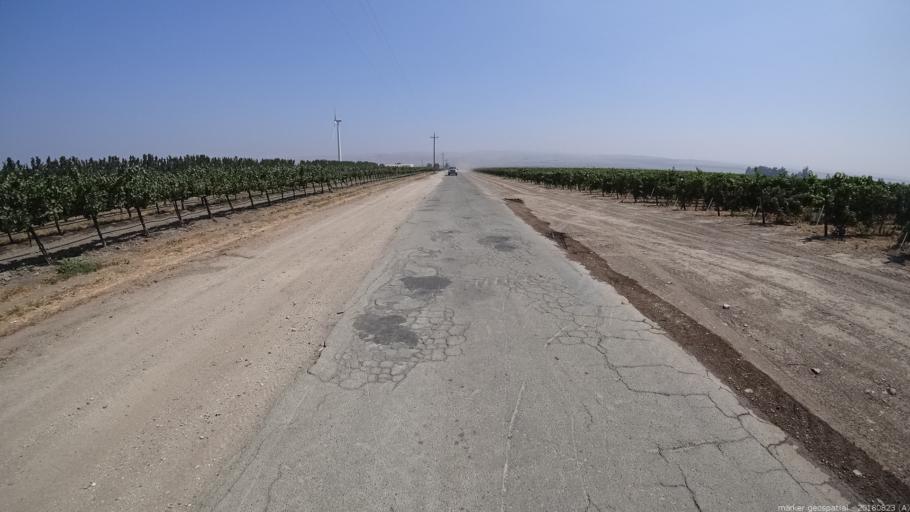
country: US
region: California
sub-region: Monterey County
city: Greenfield
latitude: 36.2706
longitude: -121.1954
